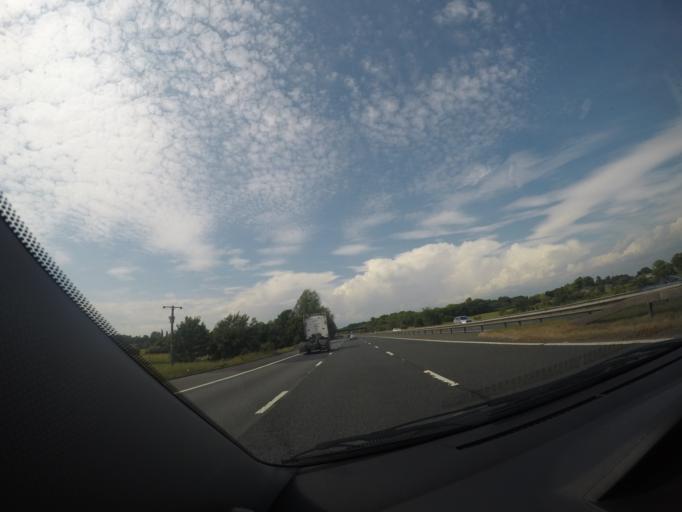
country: GB
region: England
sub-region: Cumbria
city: Carlisle
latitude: 54.9169
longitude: -2.9048
